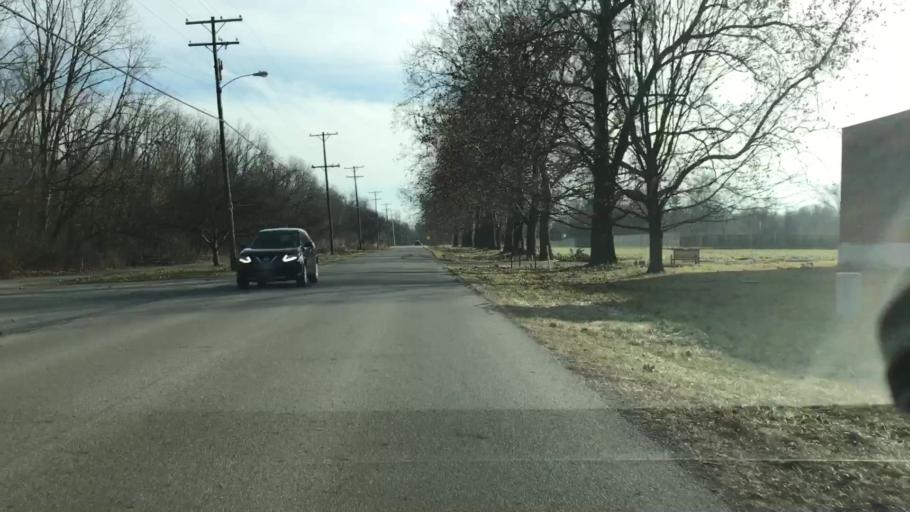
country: US
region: Ohio
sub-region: Greene County
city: Yellow Springs
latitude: 39.7982
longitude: -83.8851
